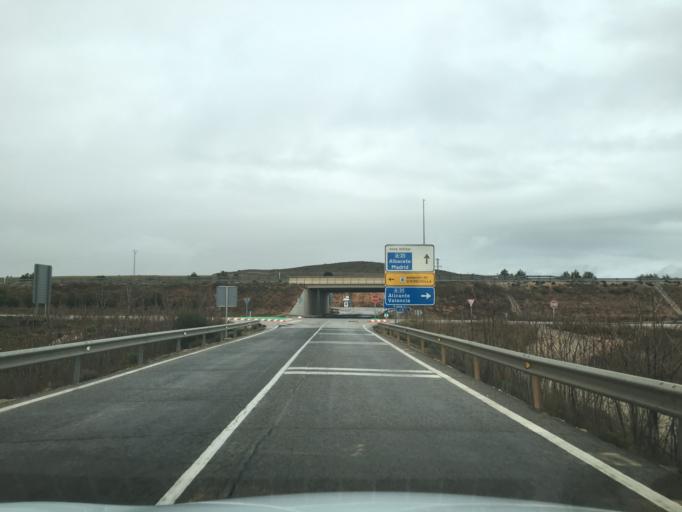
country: ES
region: Castille-La Mancha
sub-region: Provincia de Albacete
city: Chinchilla de Monte Aragon
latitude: 38.9054
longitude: -1.6917
